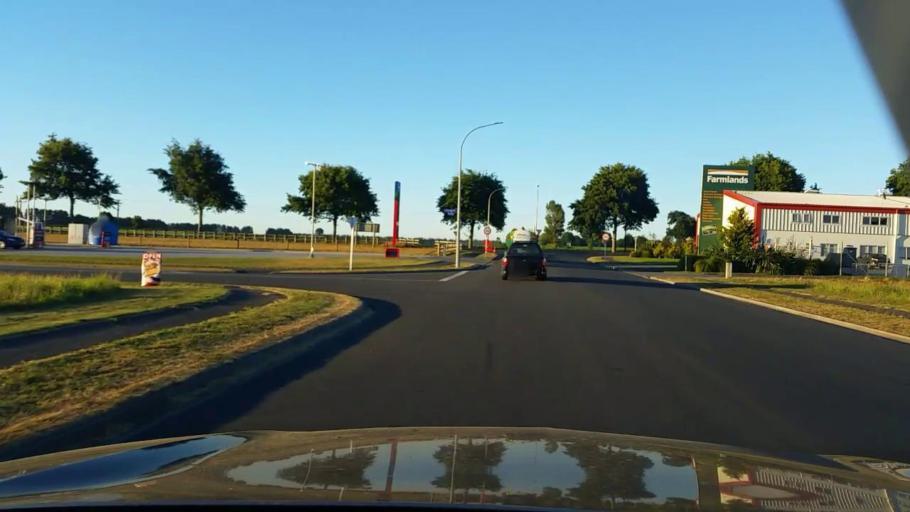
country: NZ
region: Waikato
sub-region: Matamata-Piako District
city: Matamata
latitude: -37.8179
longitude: 175.7963
